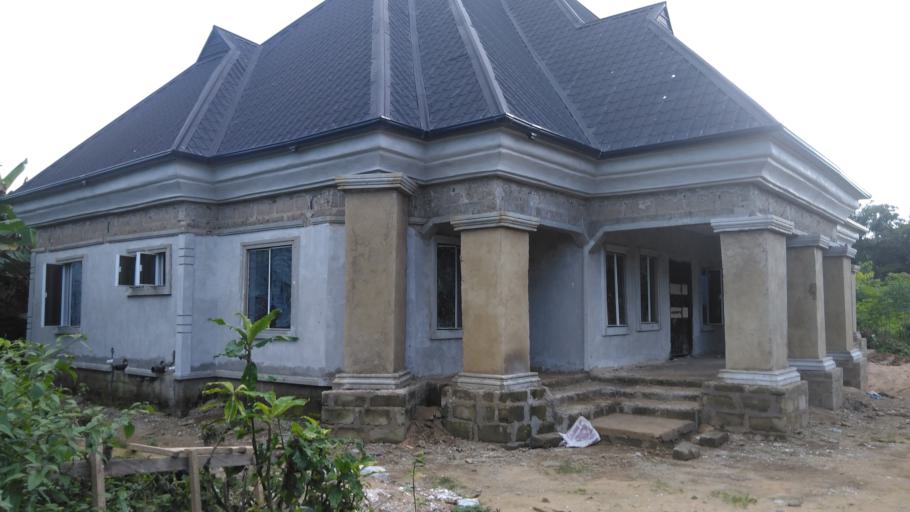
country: NG
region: Edo
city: Siluko
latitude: 6.1427
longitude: 5.2026
